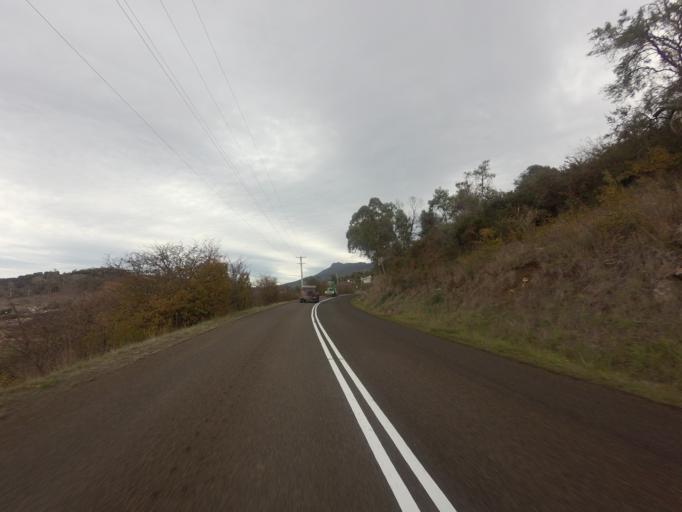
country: AU
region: Tasmania
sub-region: Brighton
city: Bridgewater
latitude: -42.6512
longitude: 147.1253
